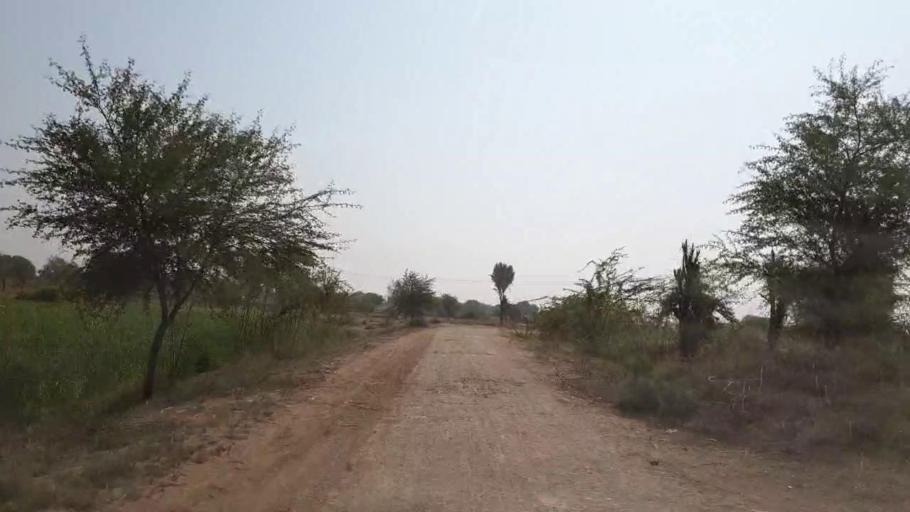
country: PK
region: Sindh
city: Mirpur Khas
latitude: 25.6290
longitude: 69.1441
